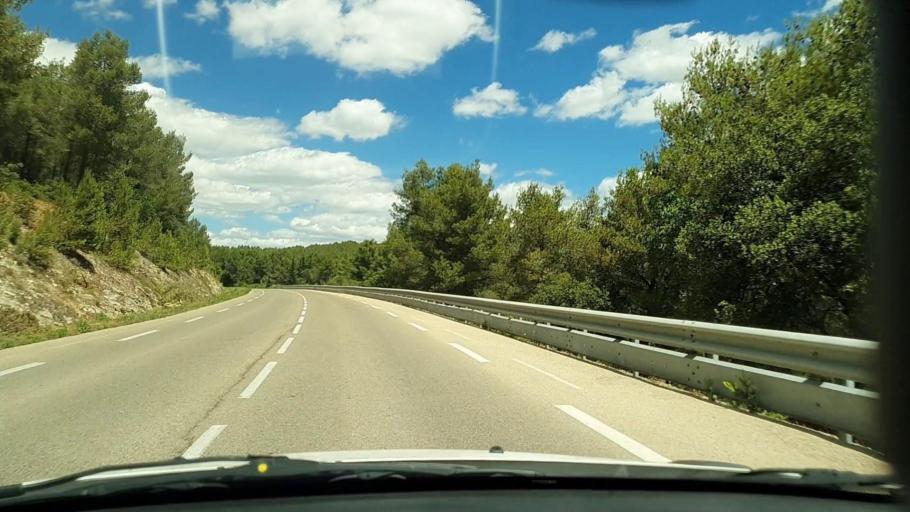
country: FR
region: Languedoc-Roussillon
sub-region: Departement du Gard
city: Poulx
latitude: 43.8796
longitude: 4.4171
